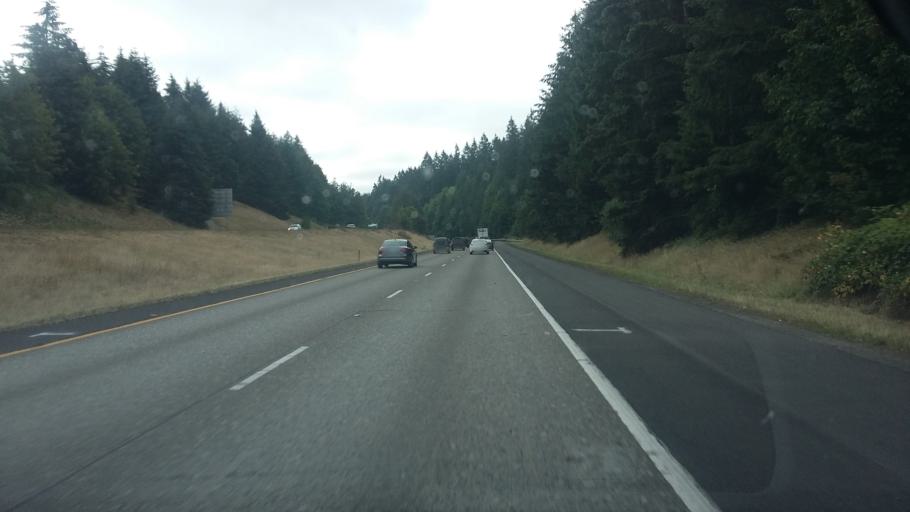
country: US
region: Washington
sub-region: Clark County
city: Salmon Creek
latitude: 45.7045
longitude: -122.6291
